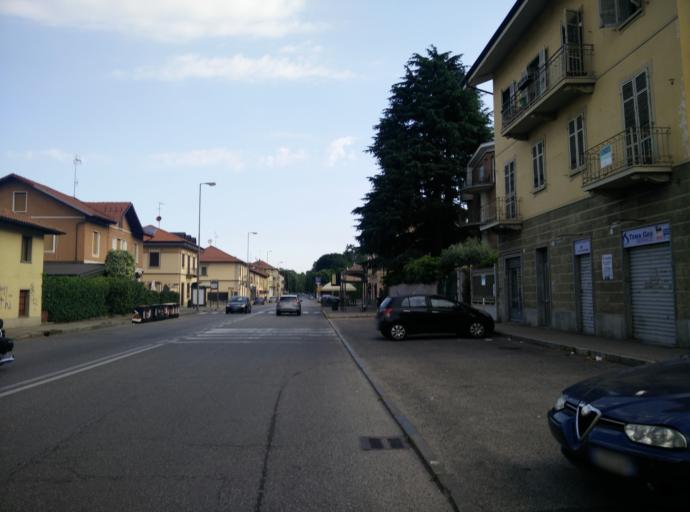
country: IT
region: Piedmont
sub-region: Provincia di Torino
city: Moncalieri
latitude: 45.0198
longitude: 7.6787
